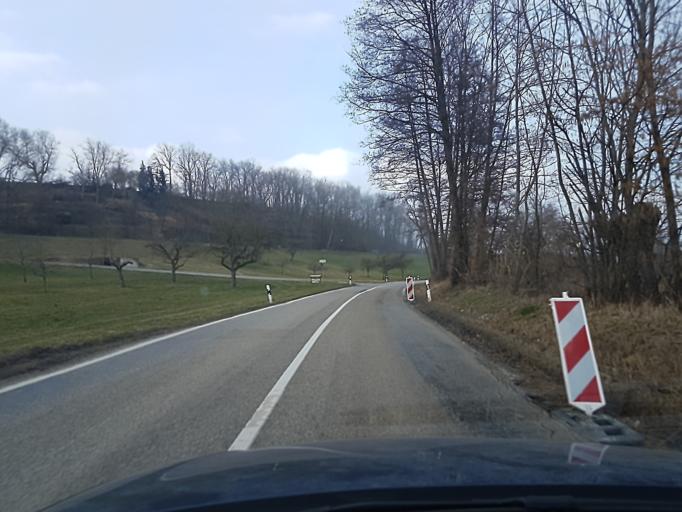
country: DE
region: Baden-Wuerttemberg
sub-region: Regierungsbezirk Stuttgart
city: Eberdingen
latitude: 48.9069
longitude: 8.9787
